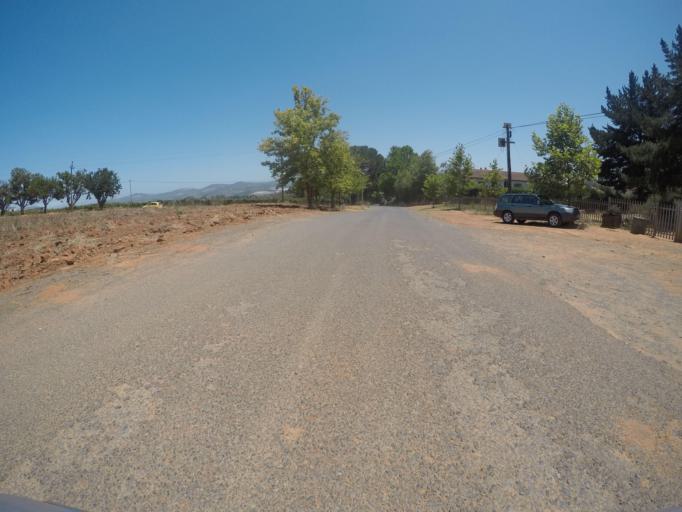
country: ZA
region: Western Cape
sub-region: Cape Winelands District Municipality
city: Stellenbosch
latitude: -33.9690
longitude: 18.8652
